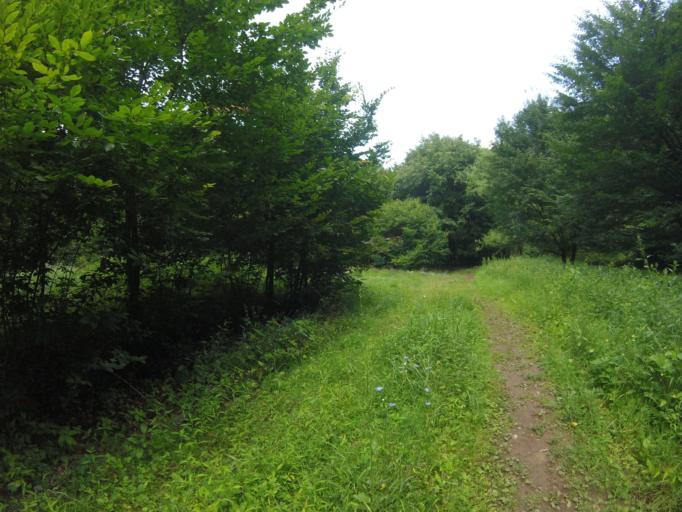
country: SK
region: Nitriansky
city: Sahy
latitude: 47.9618
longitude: 18.8979
